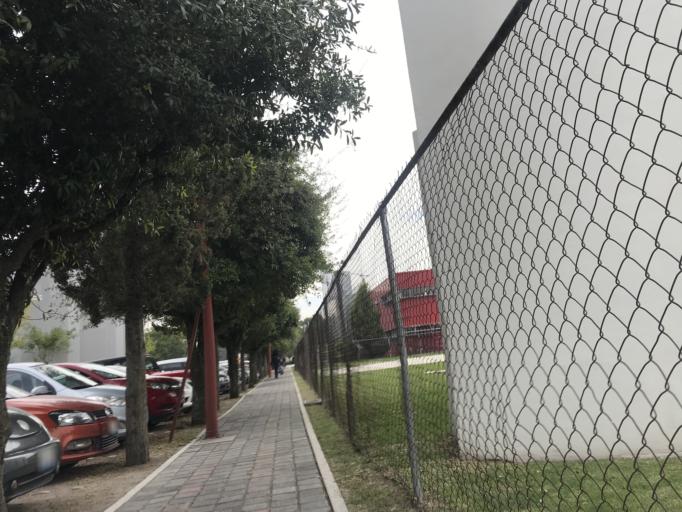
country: MX
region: Puebla
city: Tlazcalancingo
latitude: 19.0302
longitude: -98.2429
